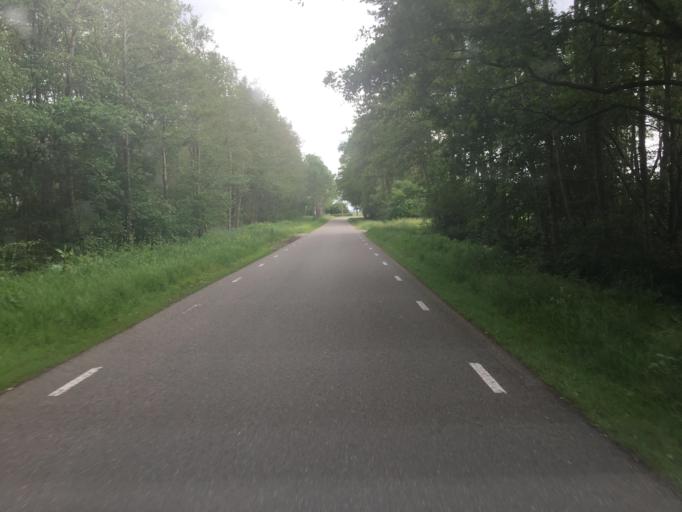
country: NL
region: Friesland
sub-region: Gemeente Heerenveen
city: Oudeschoot
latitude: 52.9111
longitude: 5.9196
